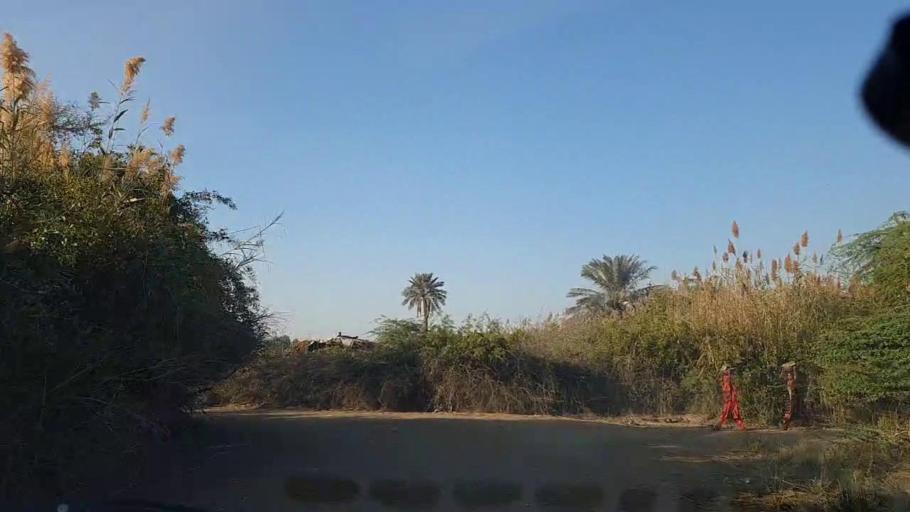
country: PK
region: Sindh
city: Berani
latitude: 25.6740
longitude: 68.9152
